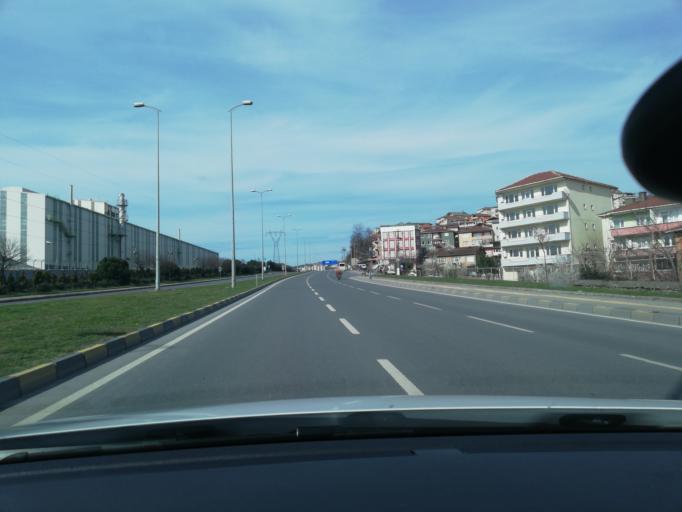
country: TR
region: Zonguldak
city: Eregli
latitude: 41.2615
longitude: 31.4354
